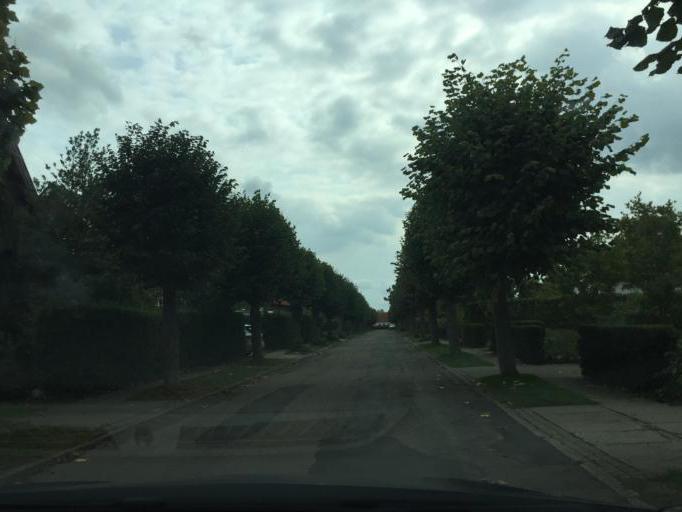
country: DK
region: South Denmark
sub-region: Odense Kommune
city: Stige
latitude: 55.4390
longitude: 10.4152
